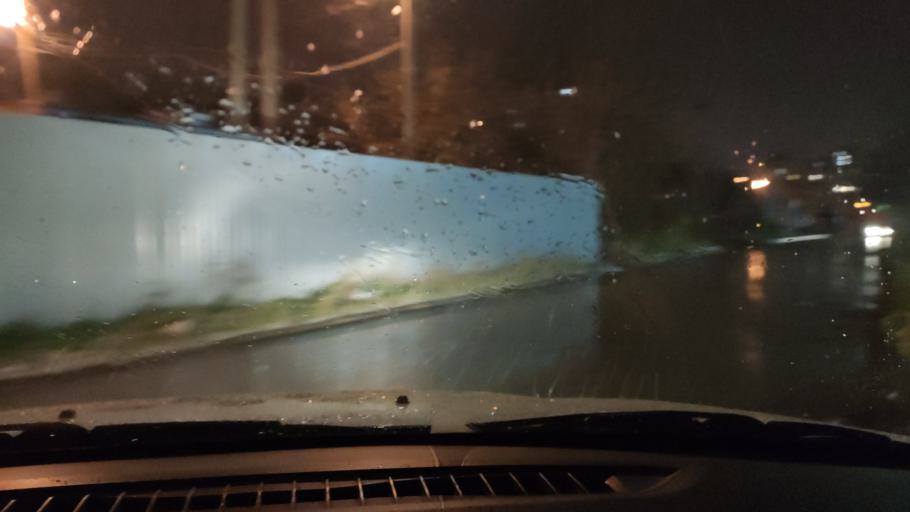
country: RU
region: Perm
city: Kondratovo
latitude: 57.9992
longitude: 56.1453
